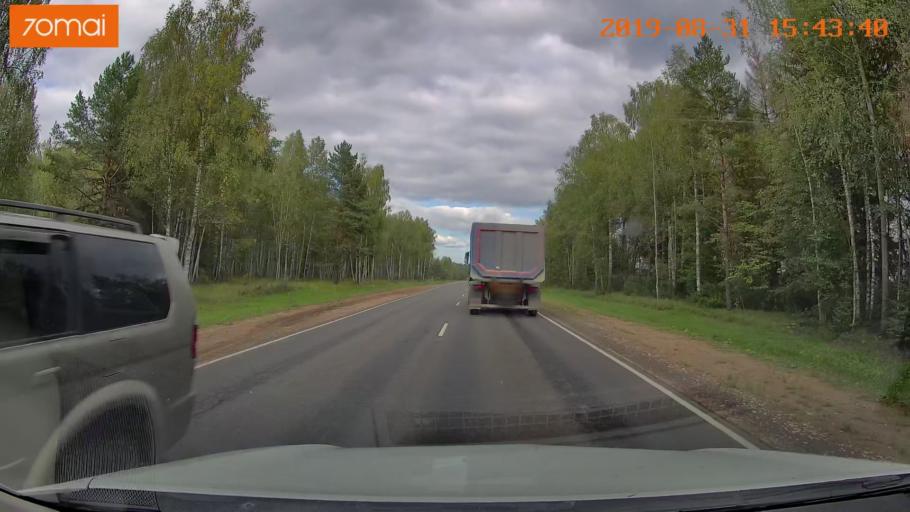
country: RU
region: Kaluga
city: Mosal'sk
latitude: 54.6540
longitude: 34.9144
